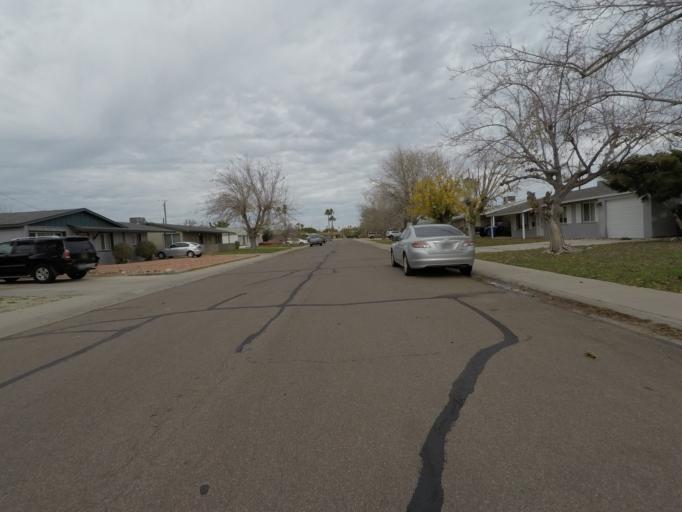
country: US
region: Arizona
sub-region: Maricopa County
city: Tempe Junction
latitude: 33.4516
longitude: -111.9326
